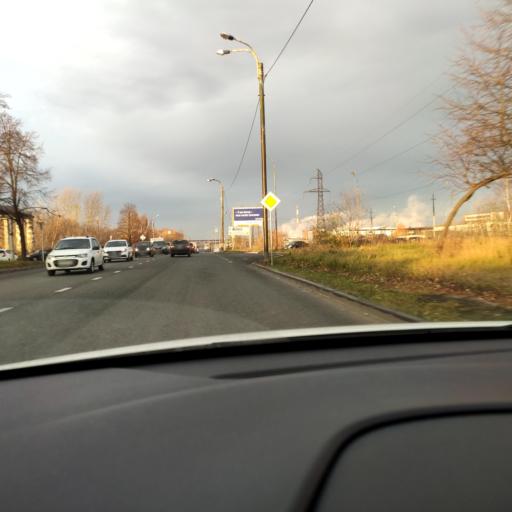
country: RU
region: Tatarstan
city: Staroye Arakchino
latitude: 55.8622
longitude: 49.0032
